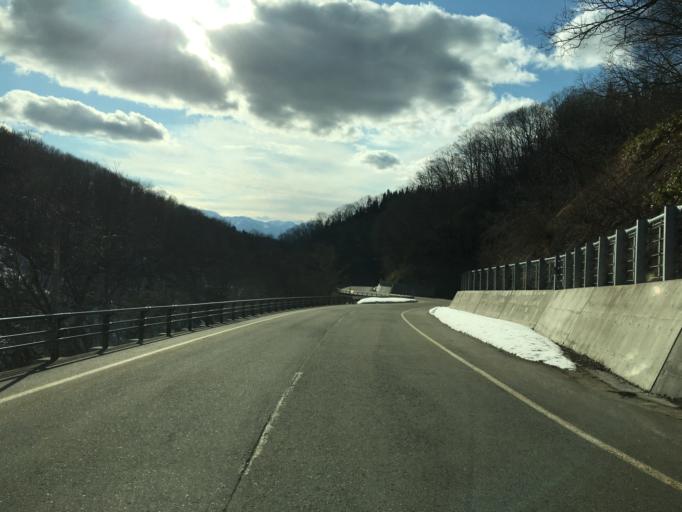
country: JP
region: Yamagata
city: Yonezawa
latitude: 37.9241
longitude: 139.9394
